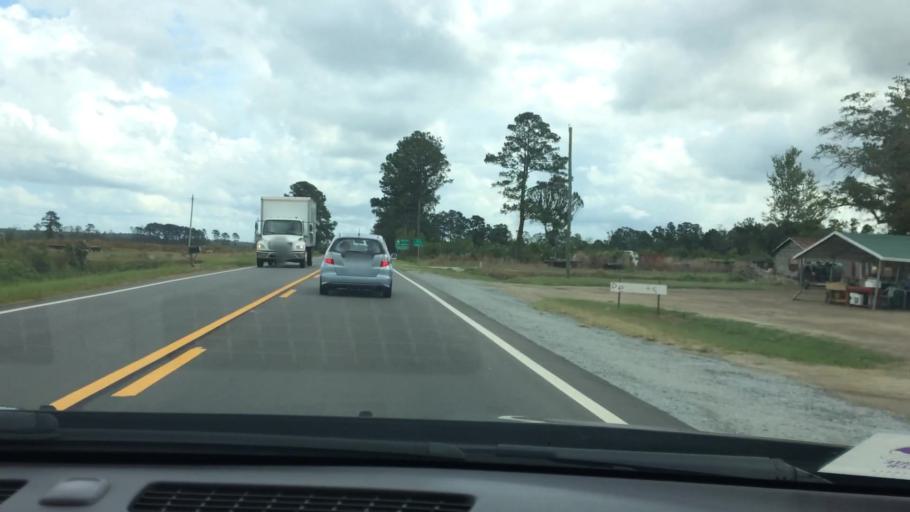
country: US
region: North Carolina
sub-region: Pitt County
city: Farmville
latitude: 35.6022
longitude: -77.6447
